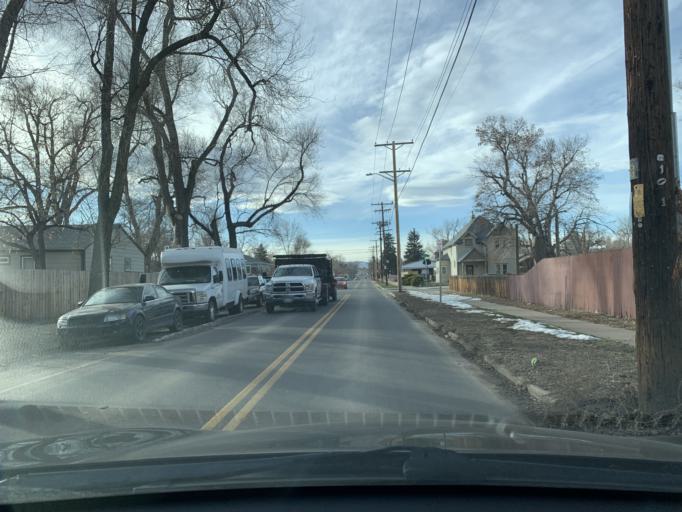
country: US
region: Colorado
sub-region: Jefferson County
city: Edgewater
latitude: 39.7330
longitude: -105.0269
